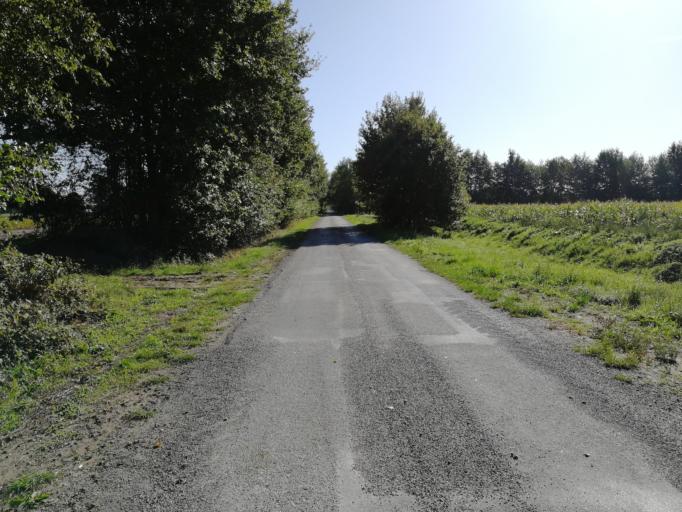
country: DE
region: Lower Saxony
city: Salzbergen
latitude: 52.3345
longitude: 7.2976
